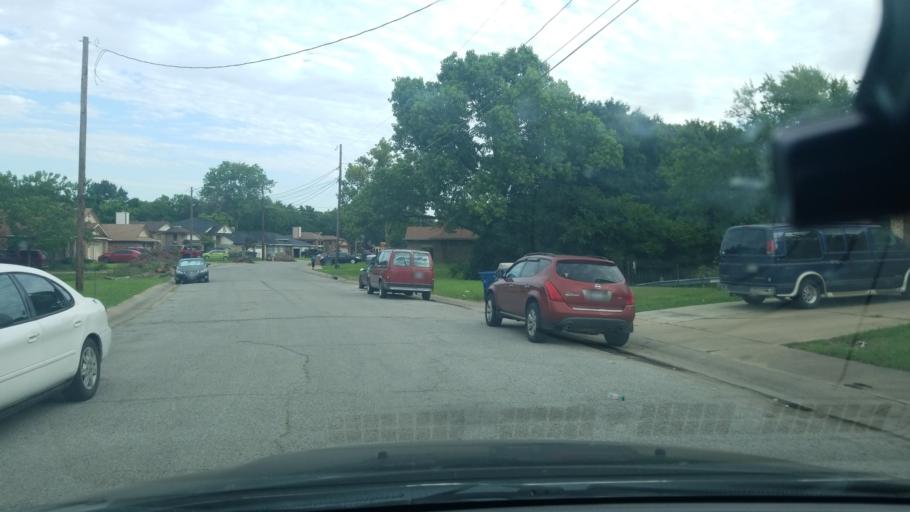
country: US
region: Texas
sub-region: Dallas County
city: Balch Springs
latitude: 32.7376
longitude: -96.6618
